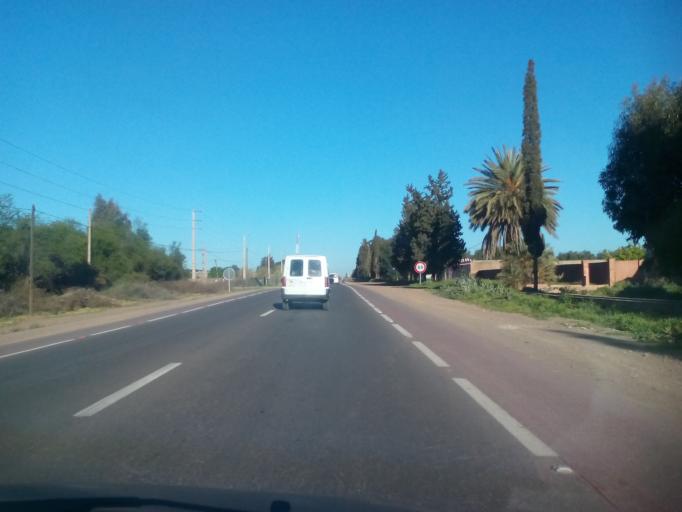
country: MA
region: Marrakech-Tensift-Al Haouz
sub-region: Marrakech
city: Marrakesh
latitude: 31.6315
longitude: -8.1851
